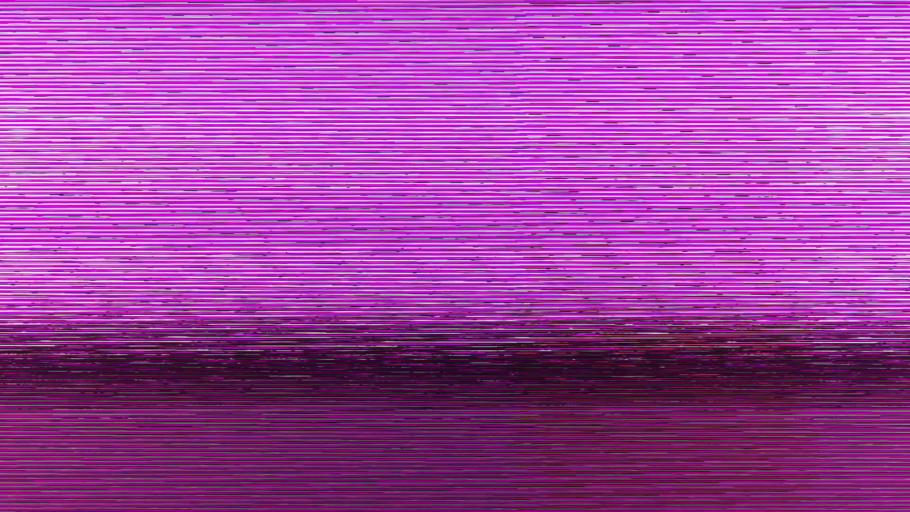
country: US
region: Michigan
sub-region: Lapeer County
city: Lapeer
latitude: 43.0352
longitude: -83.3617
